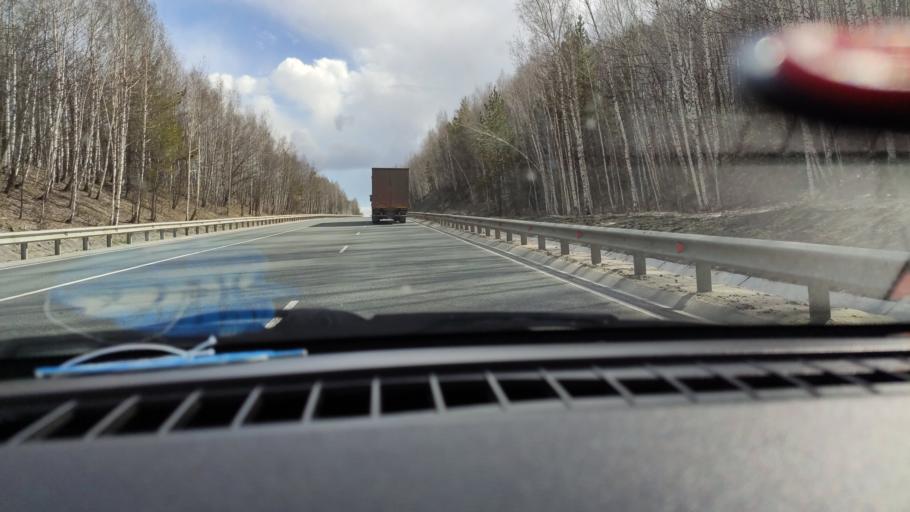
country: RU
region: Saratov
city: Khvalynsk
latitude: 52.5003
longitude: 48.0148
